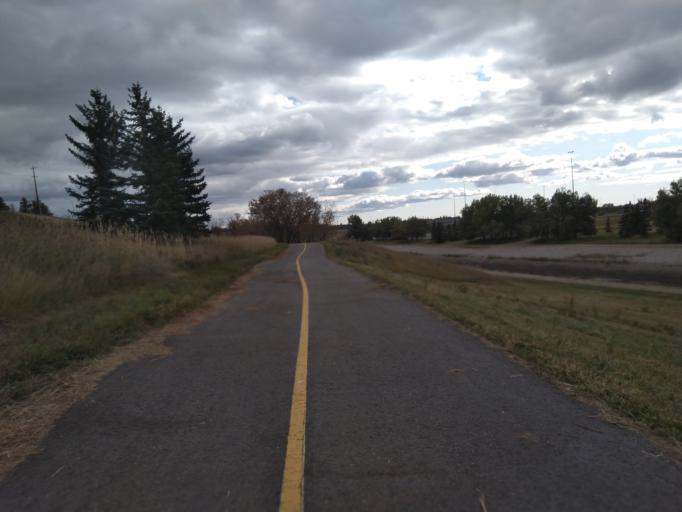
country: CA
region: Alberta
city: Calgary
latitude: 51.0403
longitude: -114.0037
